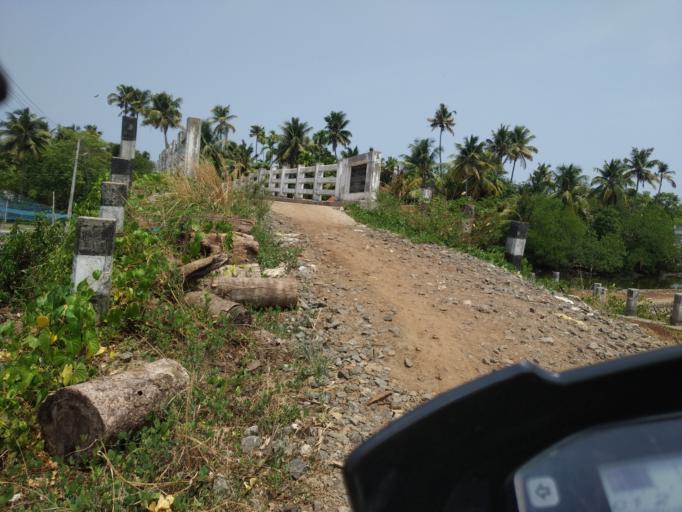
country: IN
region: Kerala
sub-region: Ernakulam
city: Elur
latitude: 10.0764
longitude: 76.2173
